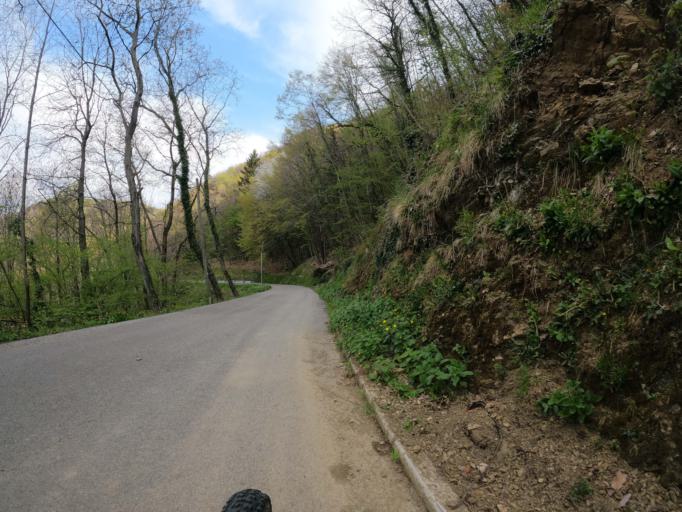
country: IT
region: Friuli Venezia Giulia
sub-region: Provincia di Udine
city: Clodig
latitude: 46.1387
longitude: 13.5922
